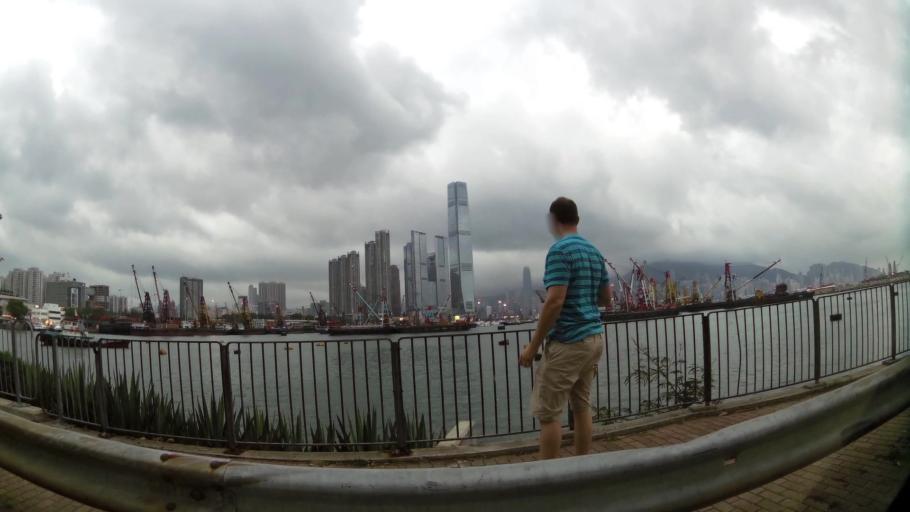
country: HK
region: Sham Shui Po
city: Sham Shui Po
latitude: 22.3169
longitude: 114.1572
